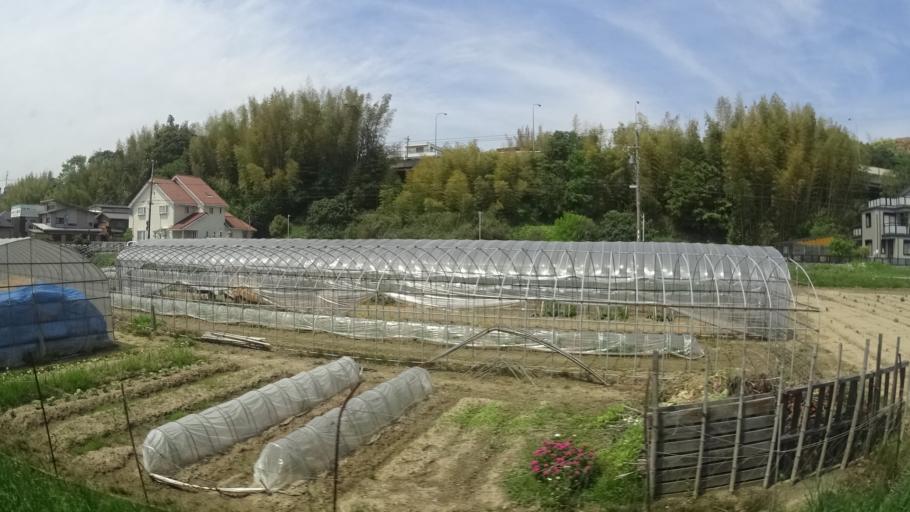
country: JP
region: Mie
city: Tsu-shi
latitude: 34.6942
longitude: 136.5083
